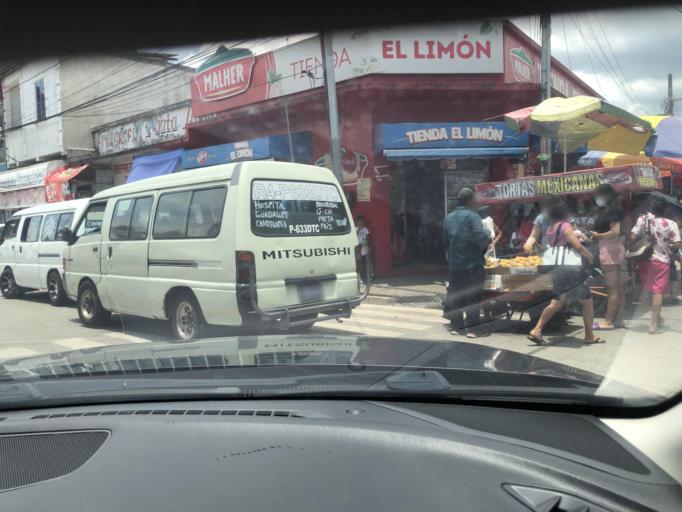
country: GT
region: Quetzaltenango
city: Coatepeque
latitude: 14.7042
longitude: -91.8642
